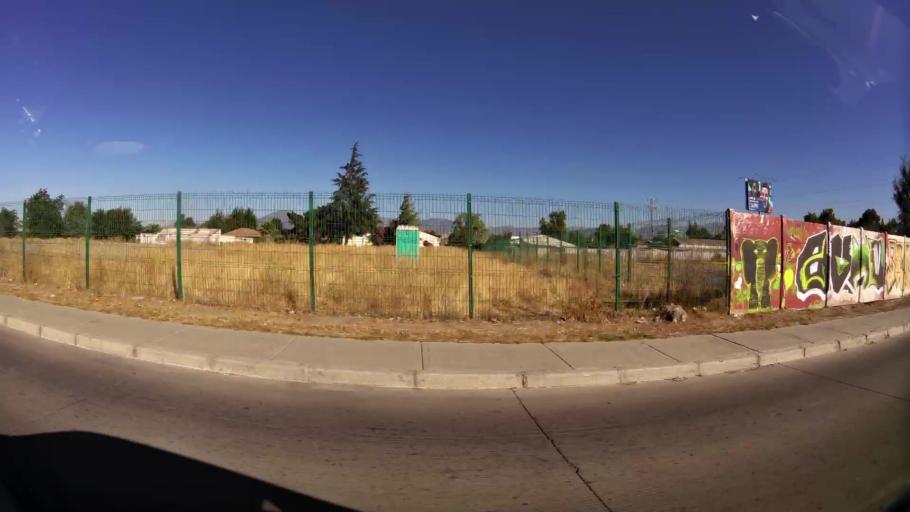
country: CL
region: O'Higgins
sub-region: Provincia de Cachapoal
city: Rancagua
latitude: -34.1840
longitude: -70.7264
